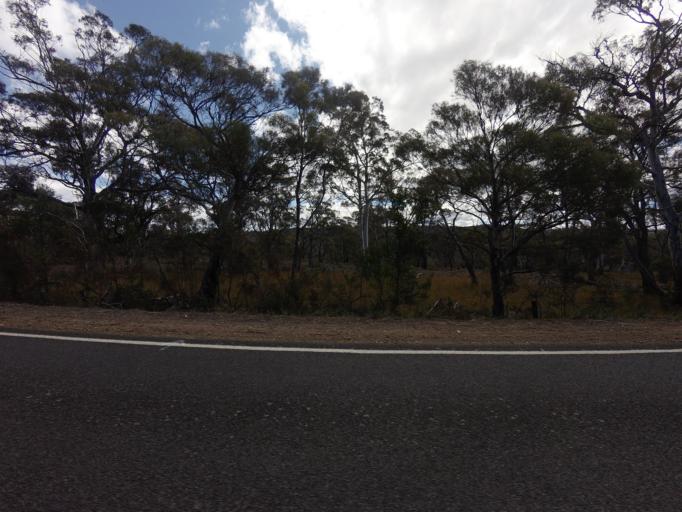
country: AU
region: Tasmania
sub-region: Break O'Day
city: St Helens
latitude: -42.0150
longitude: 147.9882
